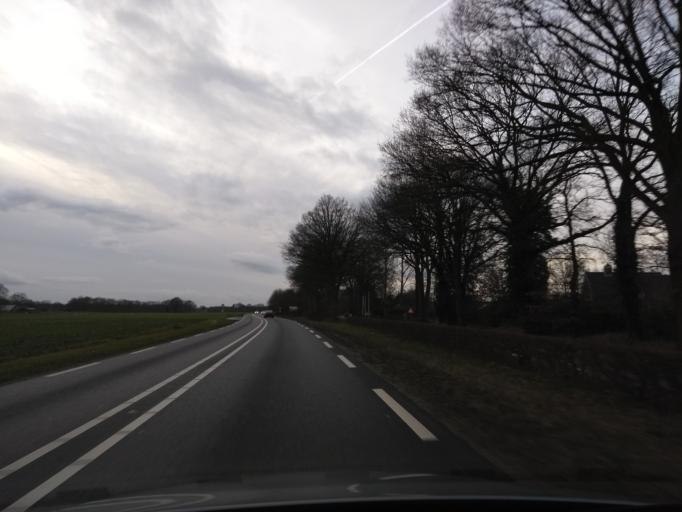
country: NL
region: Overijssel
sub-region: Gemeente Tubbergen
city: Tubbergen
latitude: 52.3657
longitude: 6.8362
